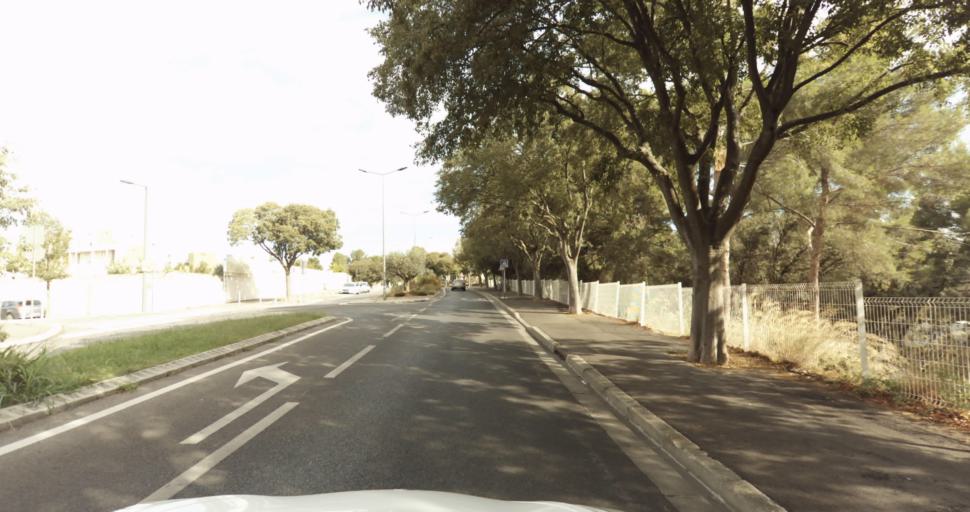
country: FR
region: Provence-Alpes-Cote d'Azur
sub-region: Departement des Bouches-du-Rhone
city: Miramas
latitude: 43.5969
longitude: 5.0113
